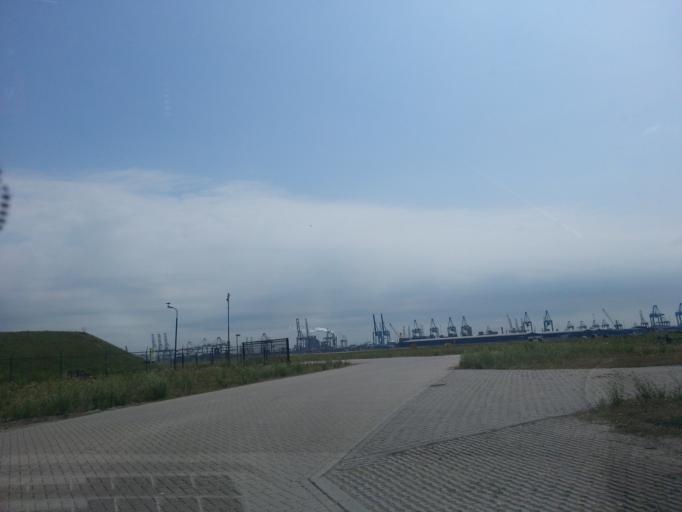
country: NL
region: South Holland
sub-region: Gemeente Rotterdam
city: Hoek van Holland
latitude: 51.9748
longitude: 4.0467
